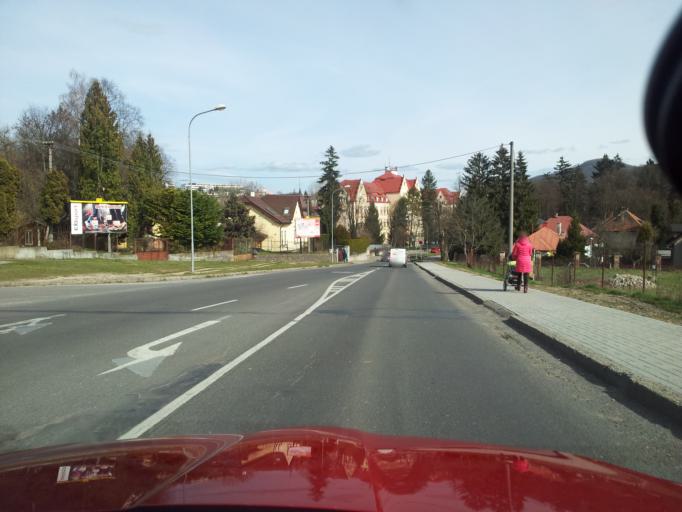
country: SK
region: Banskobystricky
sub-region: Okres Banska Bystrica
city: Banska Bystrica
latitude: 48.7386
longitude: 19.1344
